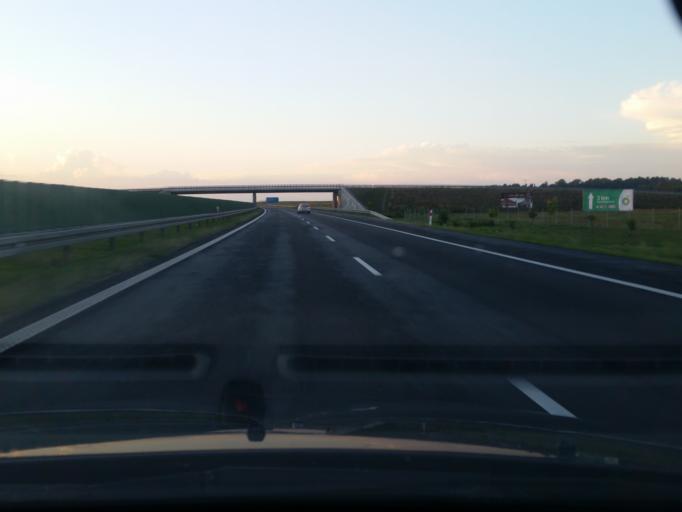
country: PL
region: Pomeranian Voivodeship
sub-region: Powiat starogardzki
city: Smetowo Graniczne
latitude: 53.7138
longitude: 18.6301
